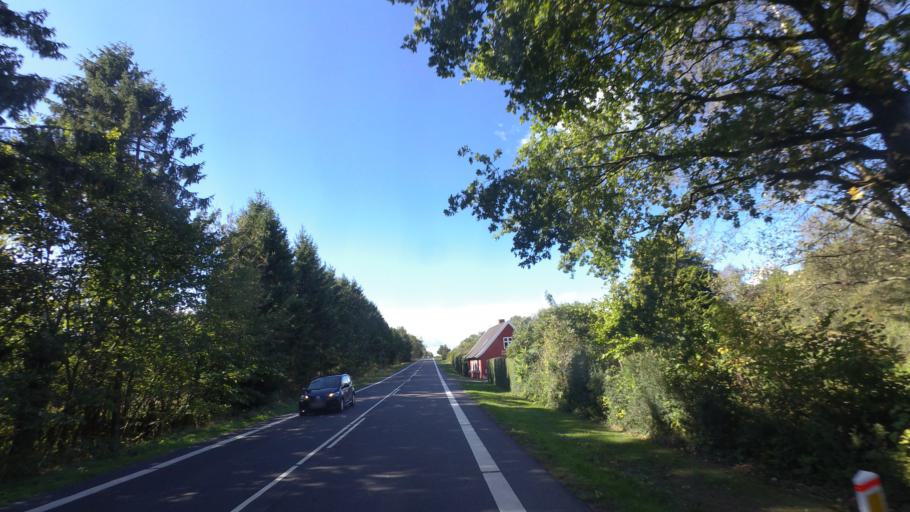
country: DK
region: Capital Region
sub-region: Bornholm Kommune
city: Akirkeby
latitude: 55.0651
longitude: 15.0131
